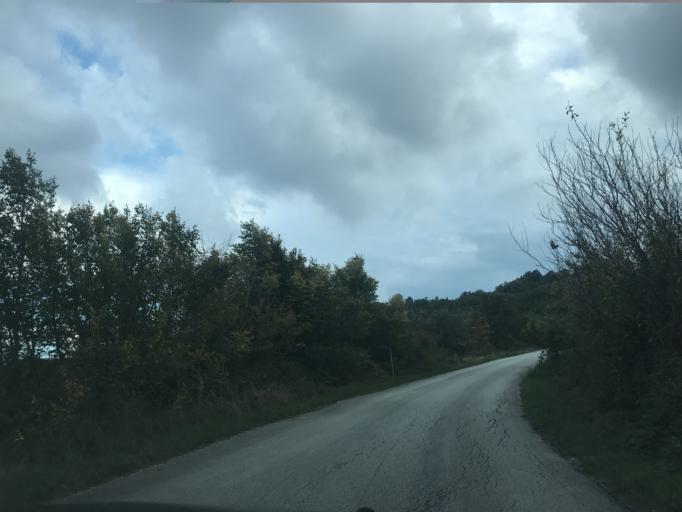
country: IT
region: Molise
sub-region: Provincia di Campobasso
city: Duronia
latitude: 41.6671
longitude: 14.4602
